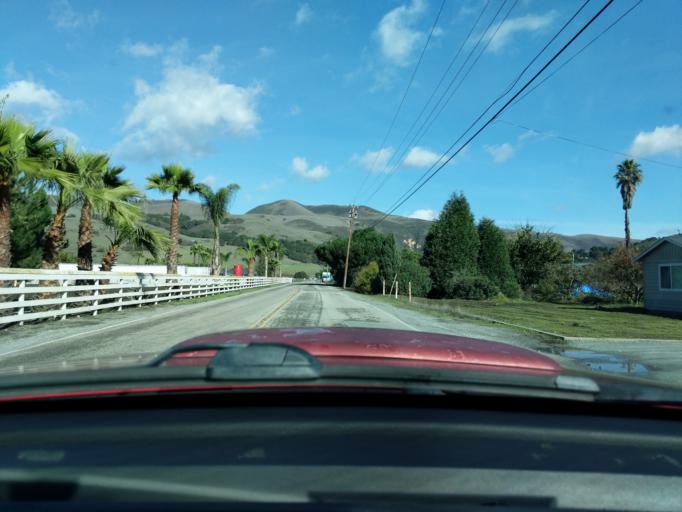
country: US
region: California
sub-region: San Benito County
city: Aromas
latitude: 36.8984
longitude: -121.6419
